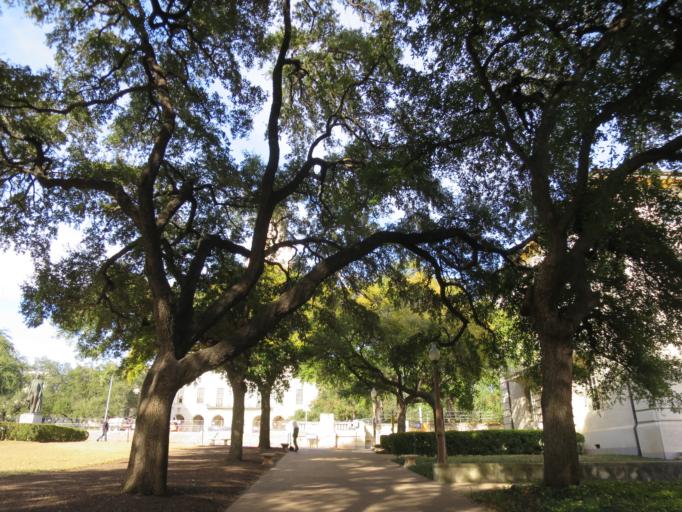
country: US
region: Texas
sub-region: Travis County
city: Austin
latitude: 30.2846
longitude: -97.7393
